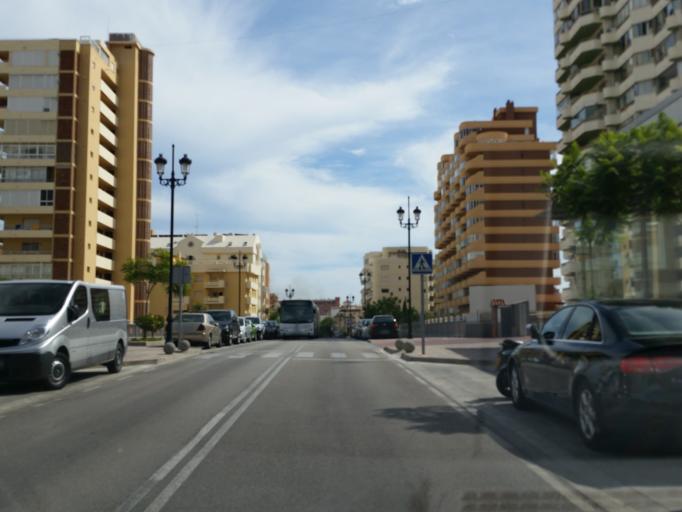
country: ES
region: Andalusia
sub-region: Provincia de Malaga
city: Fuengirola
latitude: 36.5568
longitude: -4.6123
